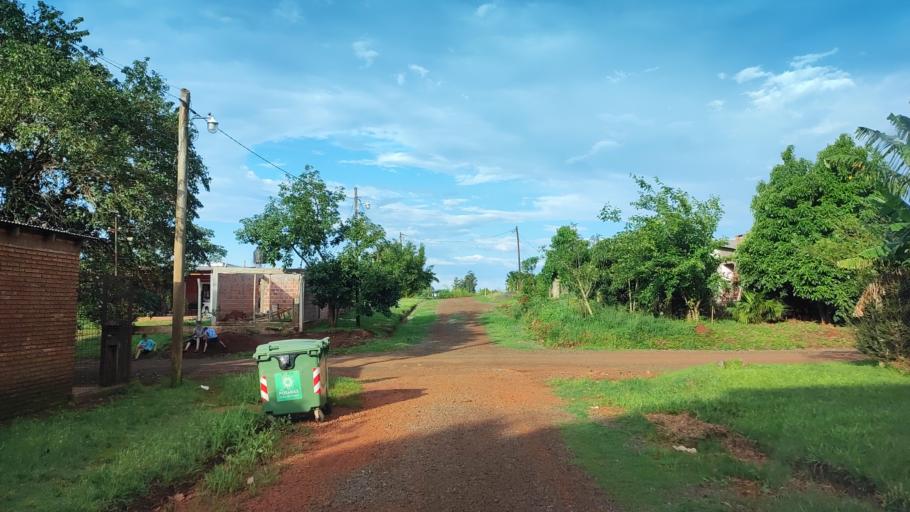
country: AR
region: Misiones
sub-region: Departamento de Capital
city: Posadas
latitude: -27.4458
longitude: -55.9613
